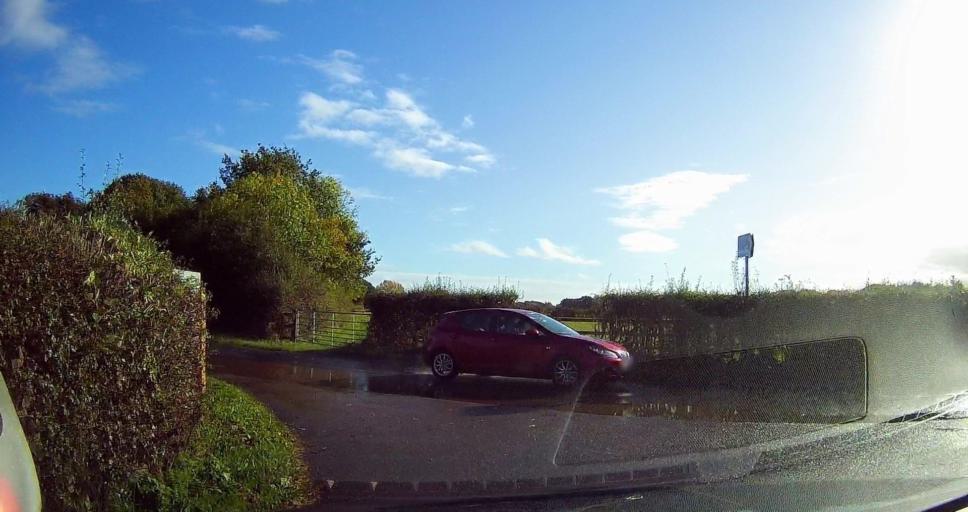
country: GB
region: England
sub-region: Staffordshire
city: Whittington
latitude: 52.6883
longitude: -1.7718
